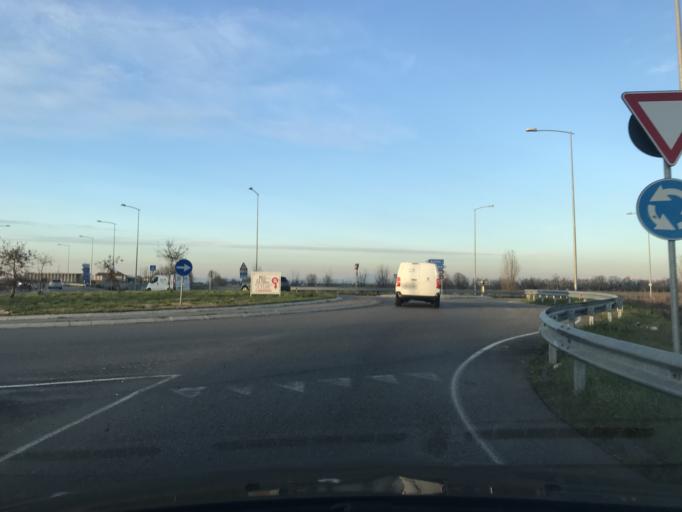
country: IT
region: Lombardy
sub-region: Provincia di Lodi
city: Marudo
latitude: 45.2708
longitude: 9.3847
